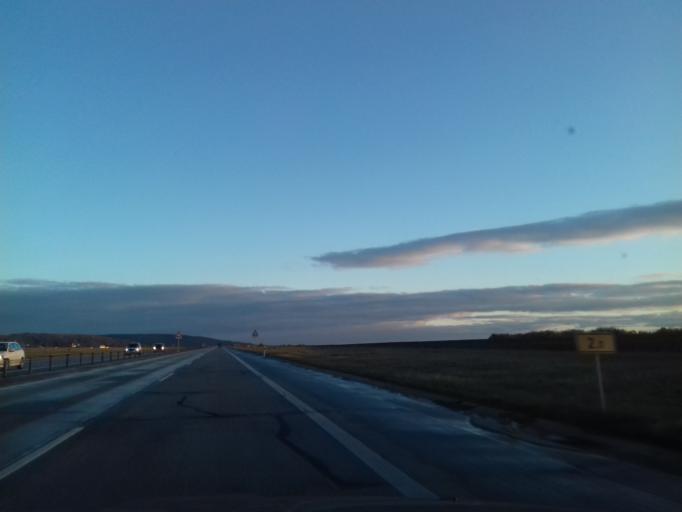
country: CZ
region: South Moravian
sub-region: Okres Vyskov
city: Vyskov
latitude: 49.2932
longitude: 17.0231
